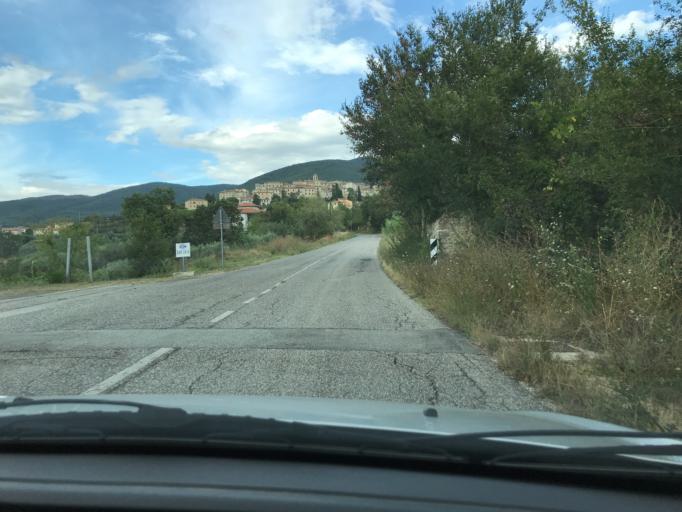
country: IT
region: Umbria
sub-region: Provincia di Terni
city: Montecchio
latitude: 42.6591
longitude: 12.2797
